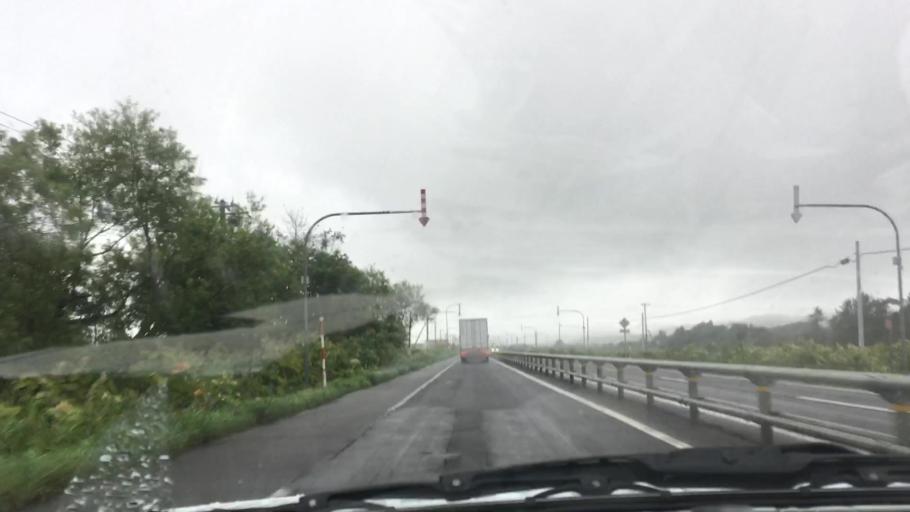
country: JP
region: Hokkaido
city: Niseko Town
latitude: 42.4188
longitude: 140.3116
